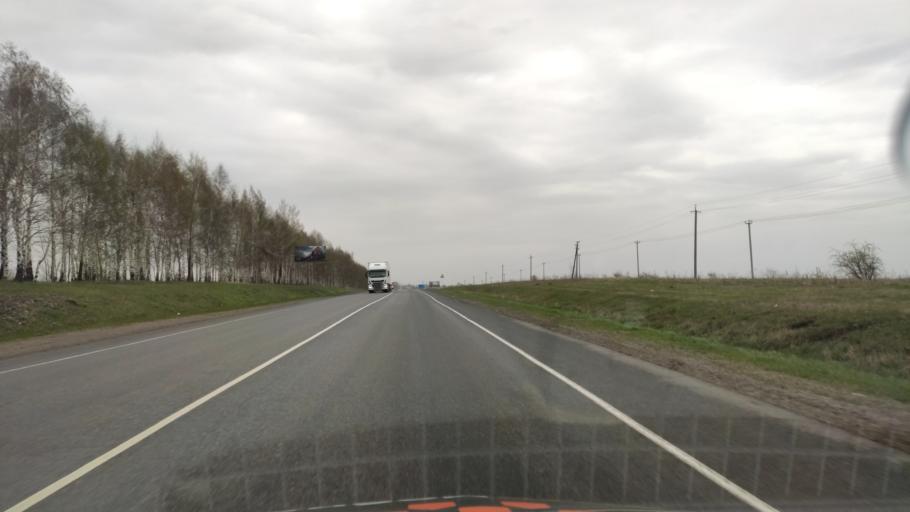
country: RU
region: Kursk
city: Gorshechnoye
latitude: 51.5036
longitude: 37.9896
